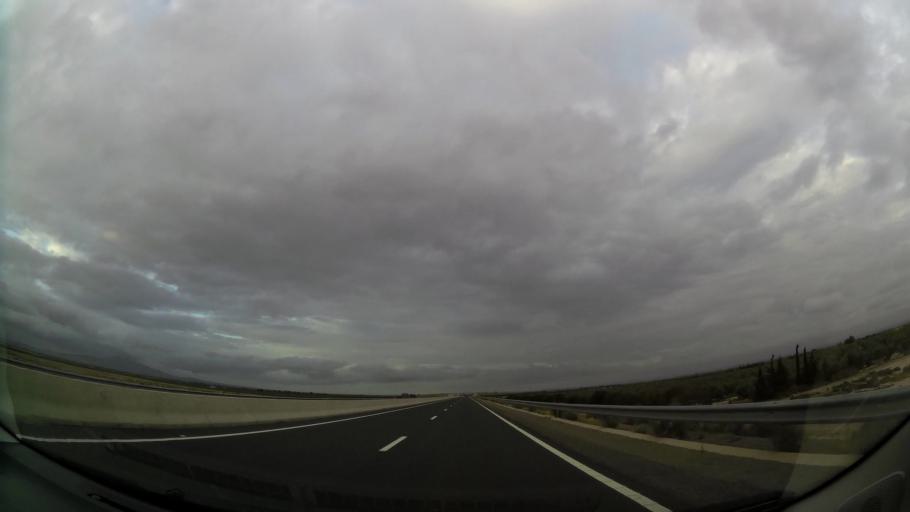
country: MA
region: Taza-Al Hoceima-Taounate
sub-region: Taza
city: Guercif
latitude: 34.3223
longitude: -3.3590
